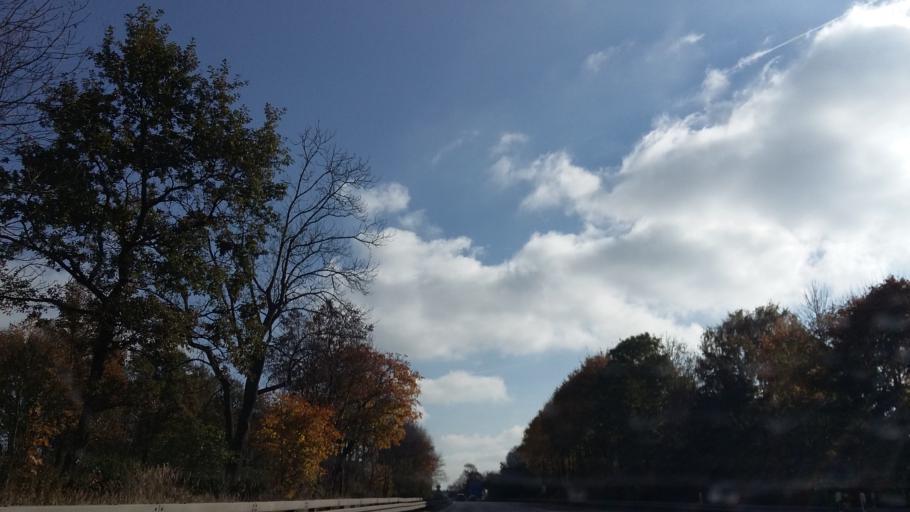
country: DE
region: Bavaria
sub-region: Upper Bavaria
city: Taufkirchen
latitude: 48.0318
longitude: 11.6142
